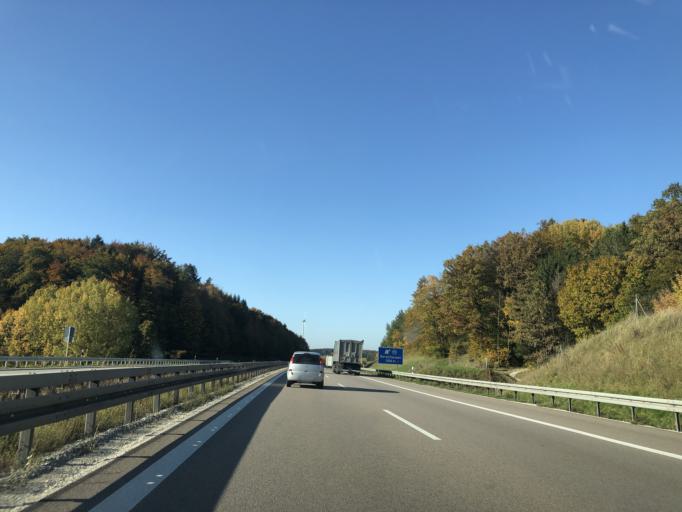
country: DE
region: Bavaria
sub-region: Upper Palatinate
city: Brunn
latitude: 49.1346
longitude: 11.8654
